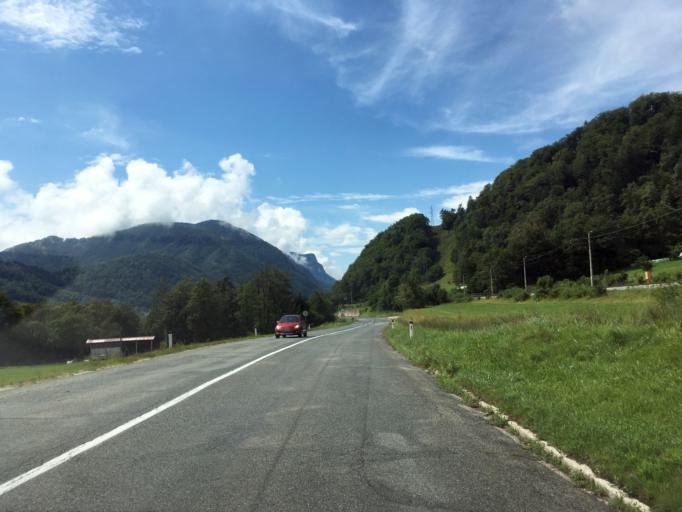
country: SI
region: Bled
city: Zasip
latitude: 46.4156
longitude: 14.1172
